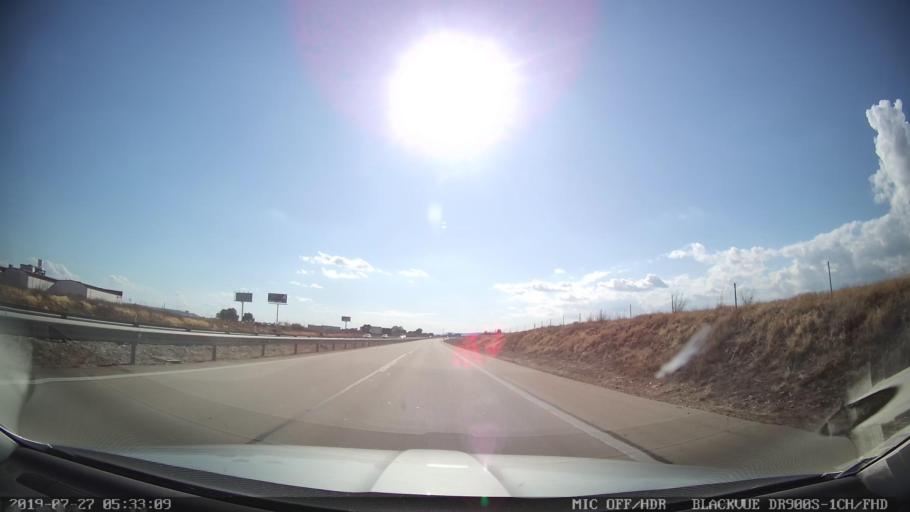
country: ES
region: Castille-La Mancha
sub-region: Province of Toledo
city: Cazalegas
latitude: 39.9819
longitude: -4.7406
